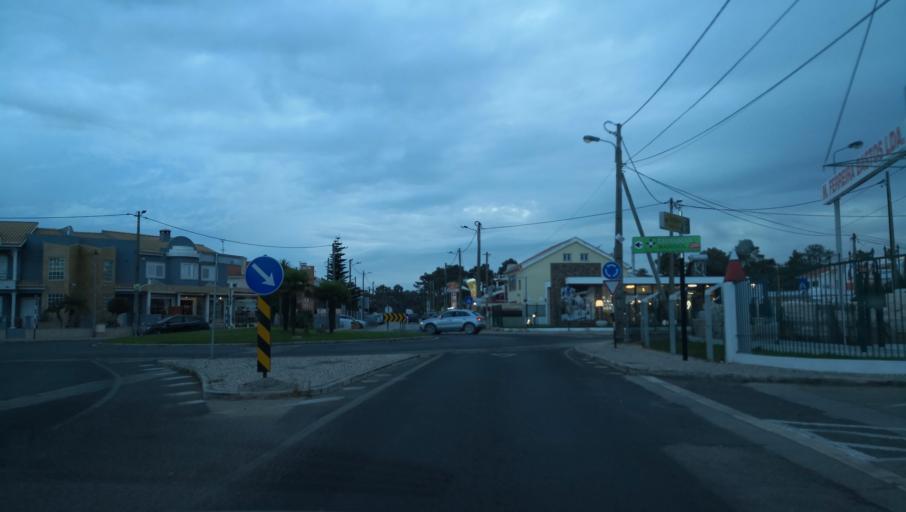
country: PT
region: Setubal
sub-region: Almada
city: Charneca
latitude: 38.6009
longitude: -9.1870
